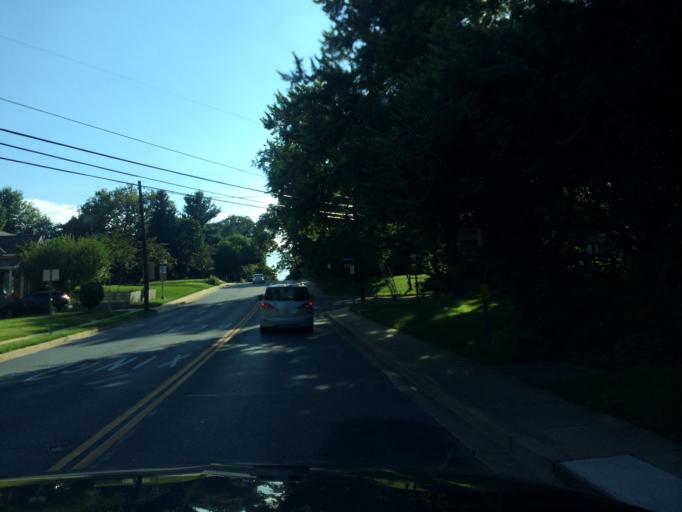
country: US
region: Maryland
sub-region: Montgomery County
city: Rockville
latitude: 39.0805
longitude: -77.1528
